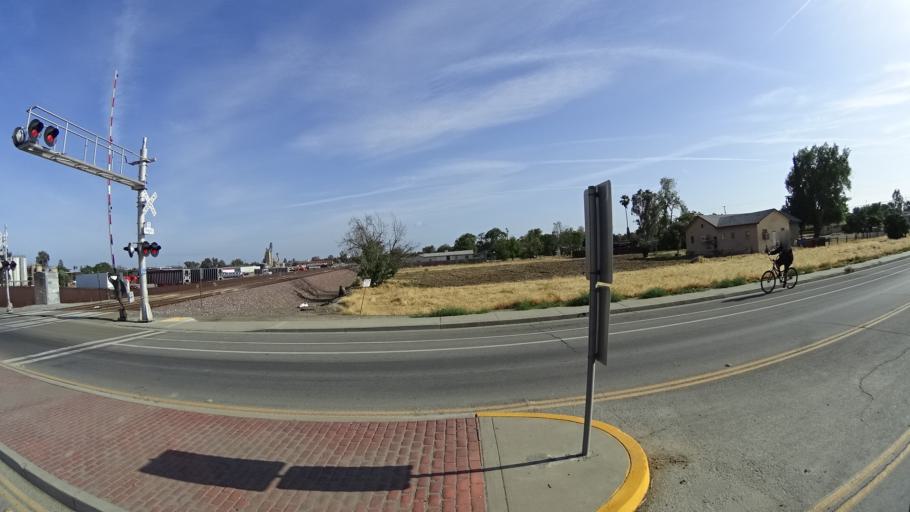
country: US
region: California
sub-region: Kings County
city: Hanford
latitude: 36.3134
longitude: -119.6494
